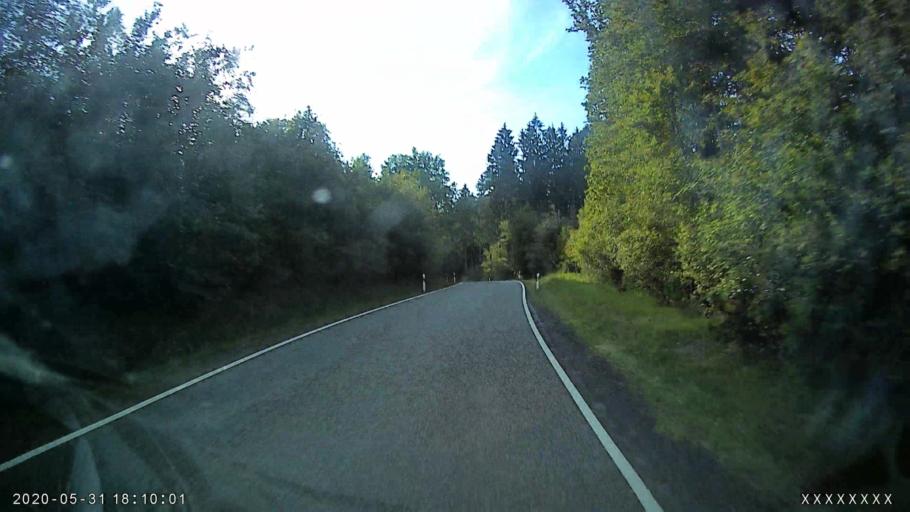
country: DE
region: Hesse
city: Dillenburg
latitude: 50.8165
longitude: 8.2606
